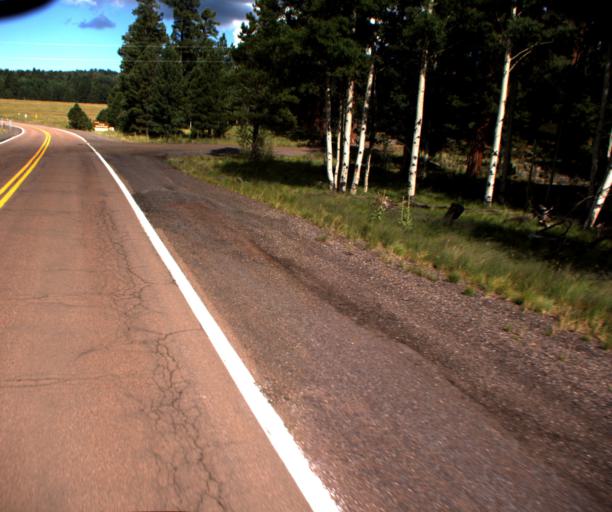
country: US
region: Arizona
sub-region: Apache County
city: Eagar
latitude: 34.0550
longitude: -109.5640
